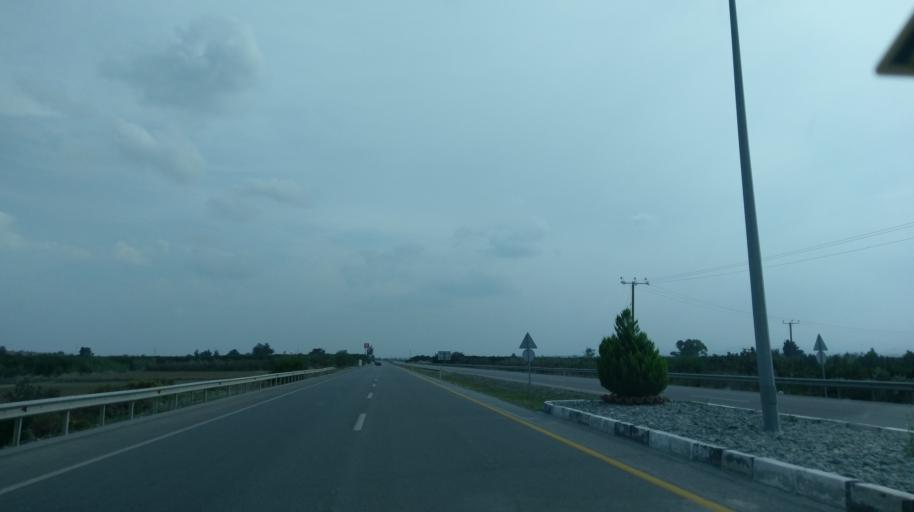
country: CY
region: Lefkosia
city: Morfou
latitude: 35.2032
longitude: 33.0455
